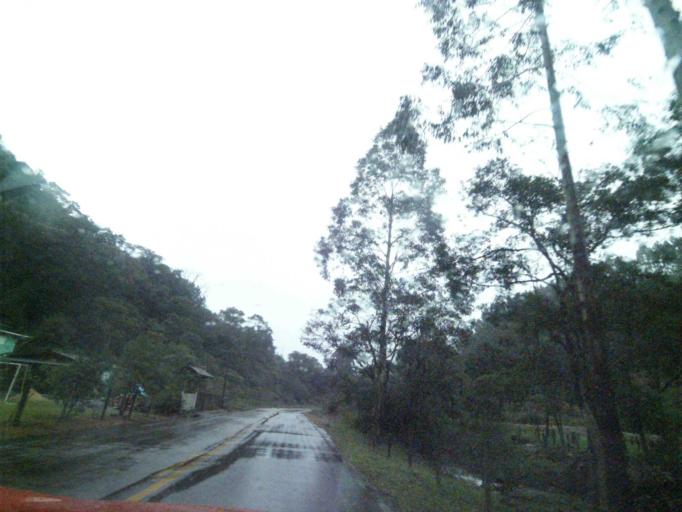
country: BR
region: Santa Catarina
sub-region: Anitapolis
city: Anitapolis
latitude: -27.8180
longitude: -49.0485
